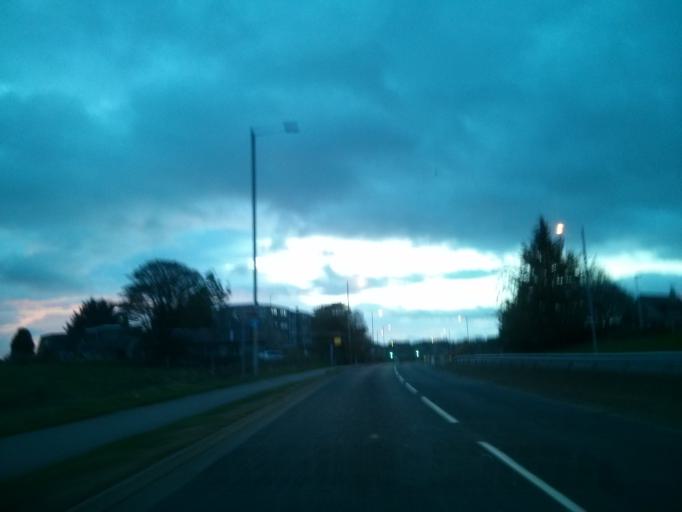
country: GB
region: Scotland
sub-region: Aberdeen City
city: Dyce
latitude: 57.1821
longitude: -2.1892
